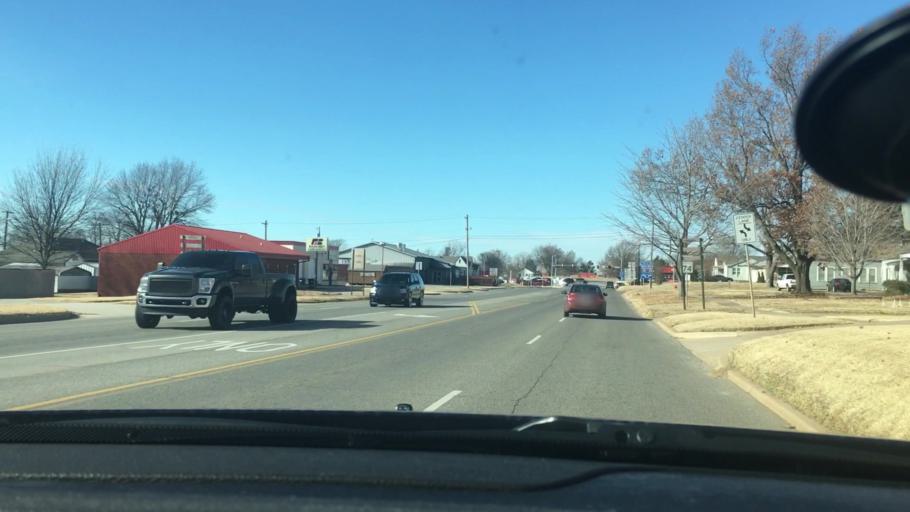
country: US
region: Oklahoma
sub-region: McClain County
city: Purcell
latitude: 35.0138
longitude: -97.3628
